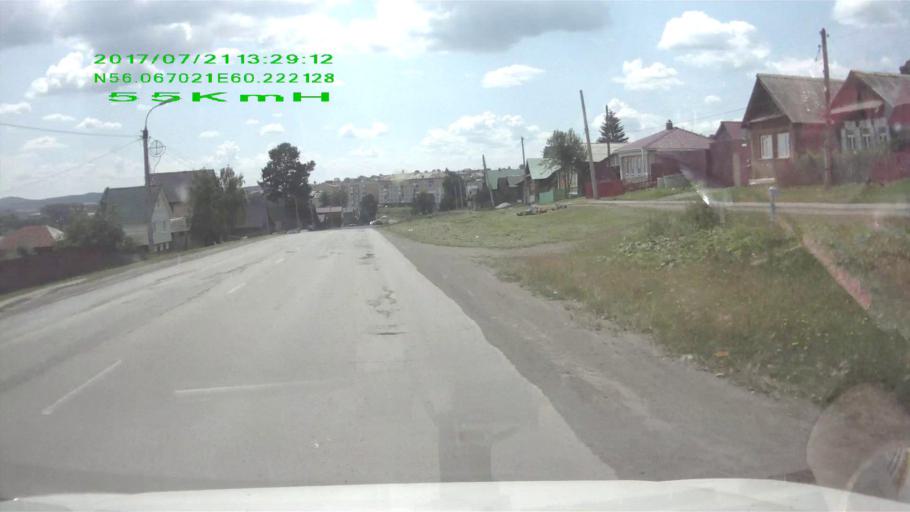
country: RU
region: Chelyabinsk
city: Verkhniy Ufaley
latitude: 56.0664
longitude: 60.2215
